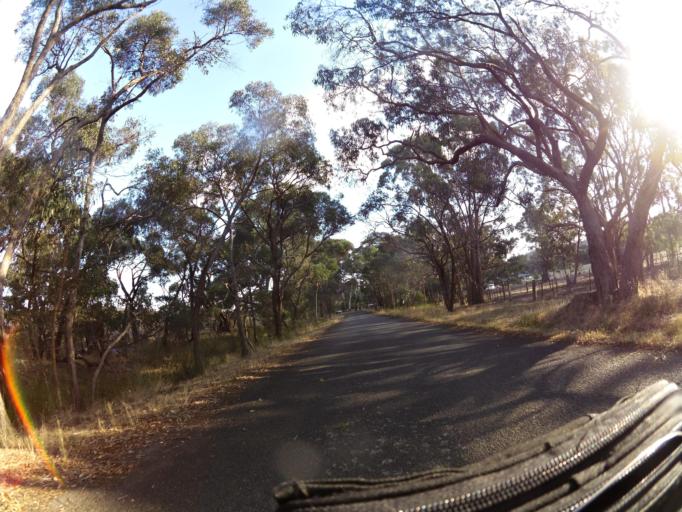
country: AU
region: Victoria
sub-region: Hume
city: Sunbury
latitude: -37.0288
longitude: 144.7972
